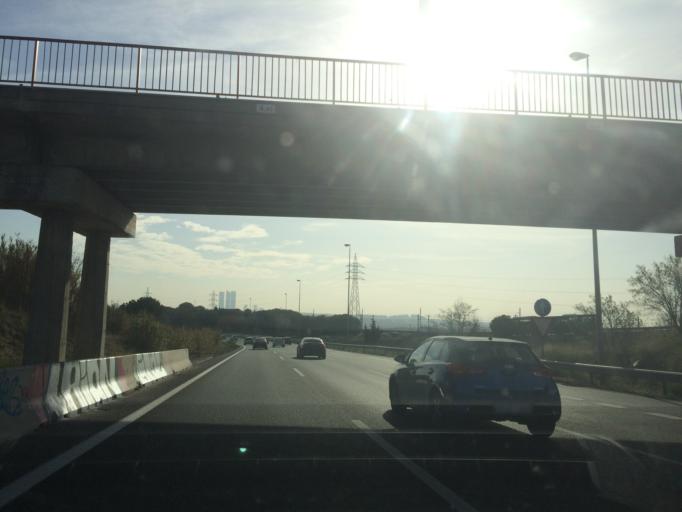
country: ES
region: Madrid
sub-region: Provincia de Madrid
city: Las Tablas
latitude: 40.5369
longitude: -3.6969
